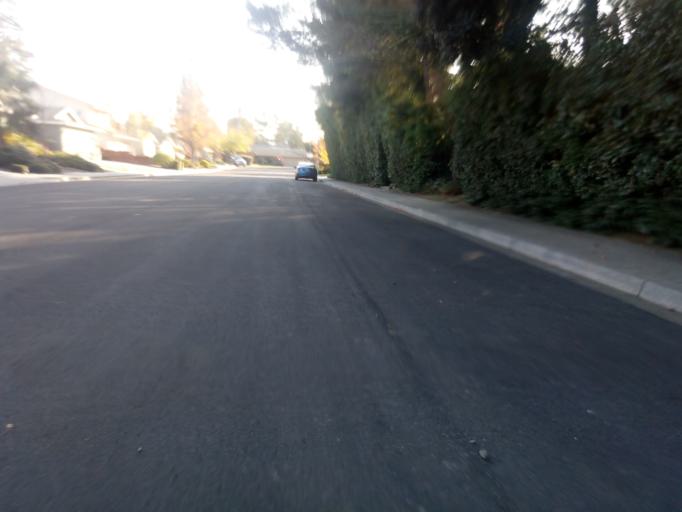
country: US
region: California
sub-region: Santa Clara County
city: Mountain View
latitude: 37.3697
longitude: -122.0712
